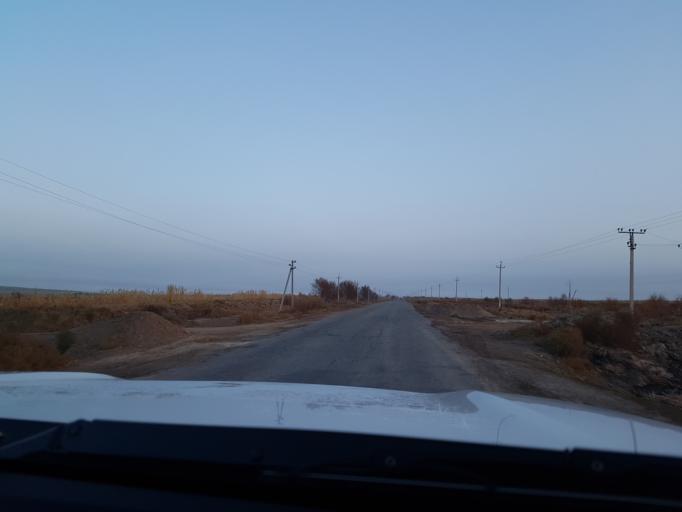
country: TM
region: Dasoguz
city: Koeneuergench
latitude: 41.7718
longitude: 58.6943
